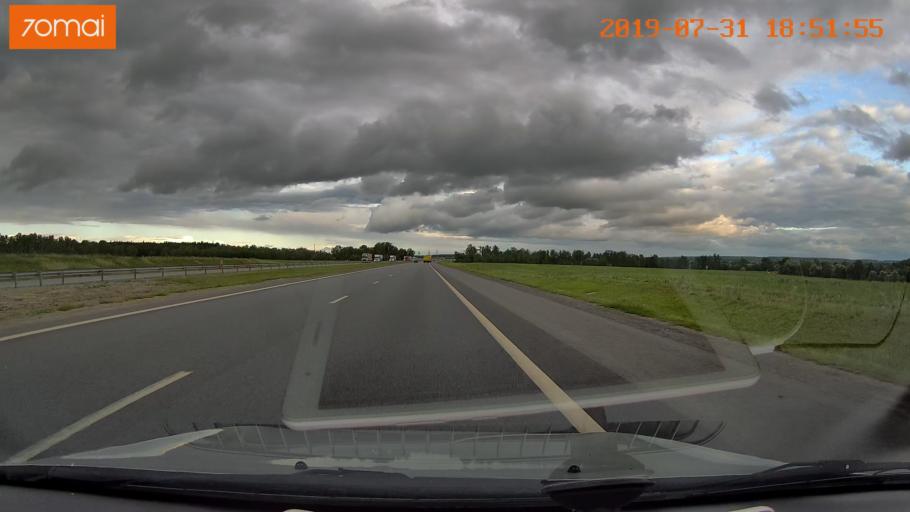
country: RU
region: Moskovskaya
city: Voskresensk
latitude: 55.2181
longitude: 38.6191
